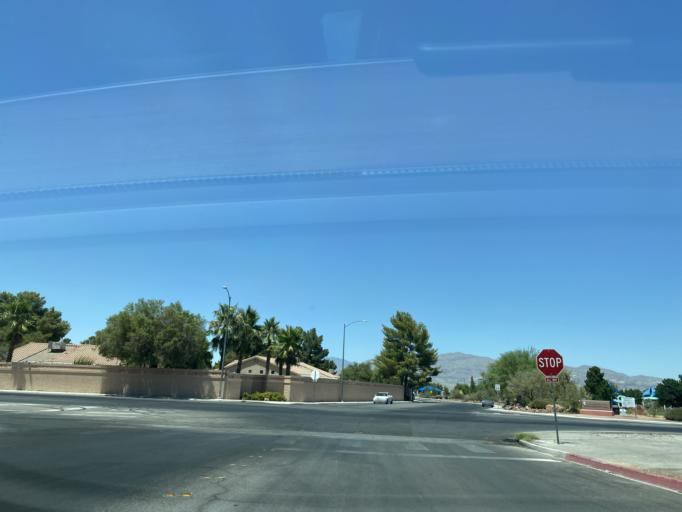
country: US
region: Nevada
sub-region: Clark County
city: Las Vegas
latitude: 36.2314
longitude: -115.2120
